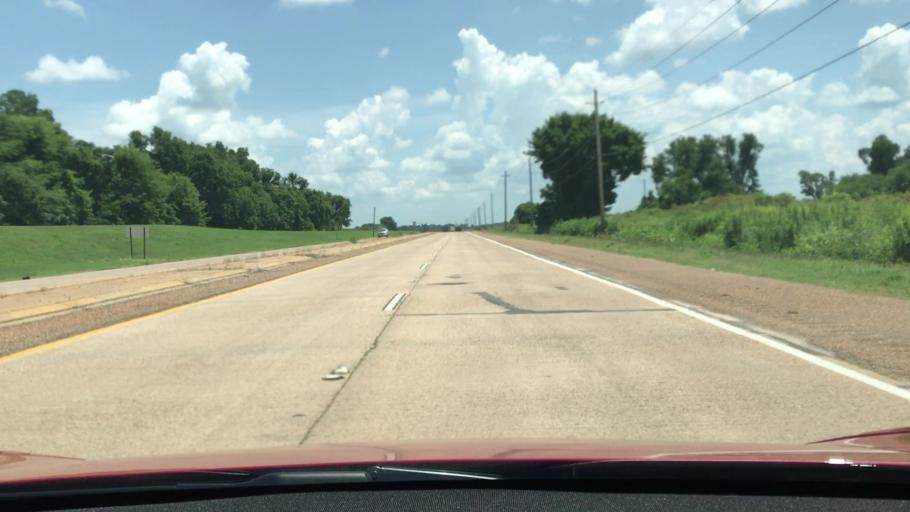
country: US
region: Louisiana
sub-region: Bossier Parish
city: Bossier City
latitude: 32.3970
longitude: -93.6899
